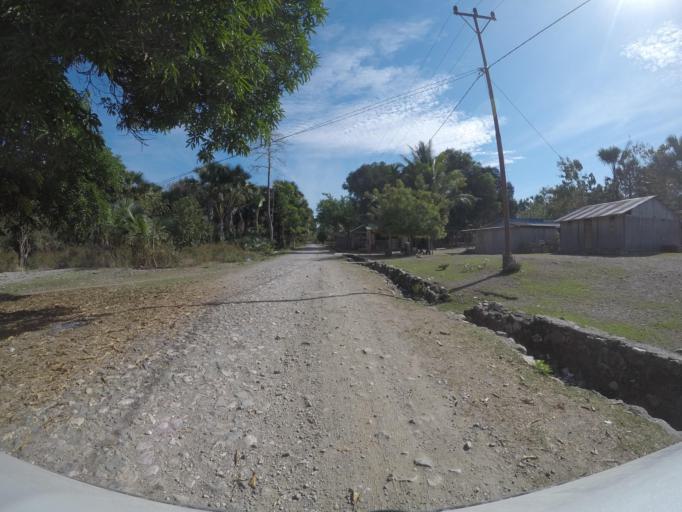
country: TL
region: Bobonaro
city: Maliana
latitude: -8.8500
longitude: 125.2187
